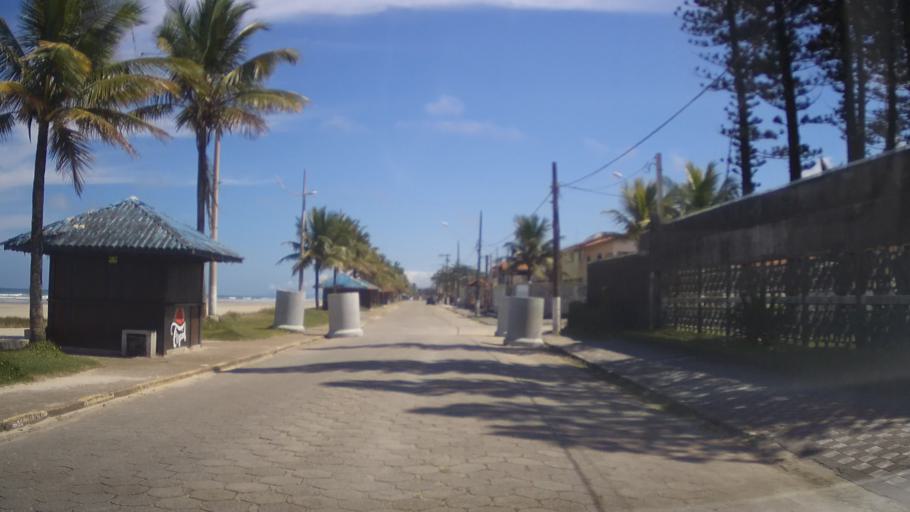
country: BR
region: Sao Paulo
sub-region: Mongagua
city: Mongagua
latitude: -24.1360
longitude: -46.6979
